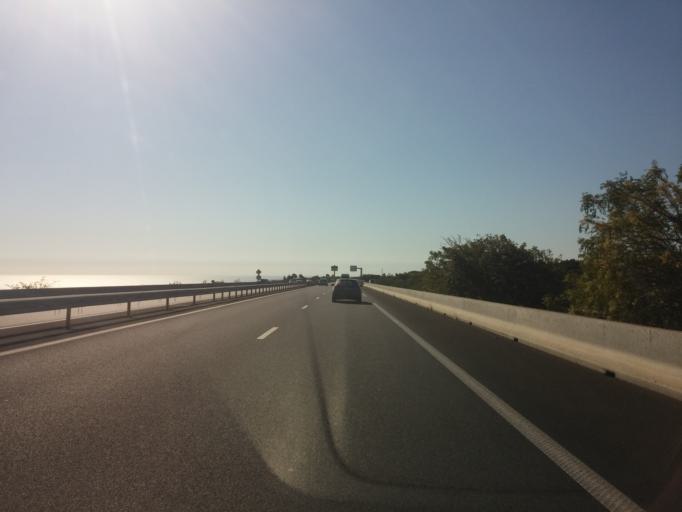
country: RE
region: Reunion
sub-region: Reunion
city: Trois-Bassins
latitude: -21.0702
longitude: 55.2496
